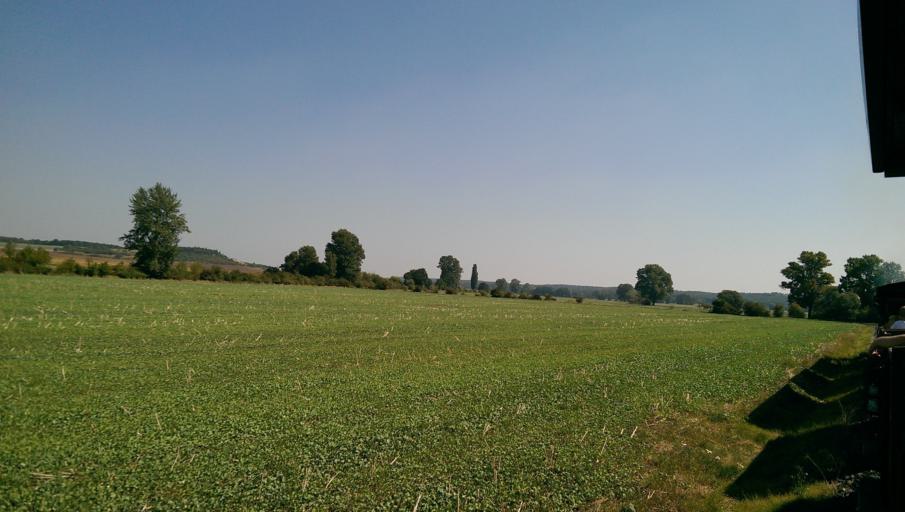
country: CZ
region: Central Bohemia
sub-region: Okres Kolin
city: Kolin
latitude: 50.0530
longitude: 15.2361
